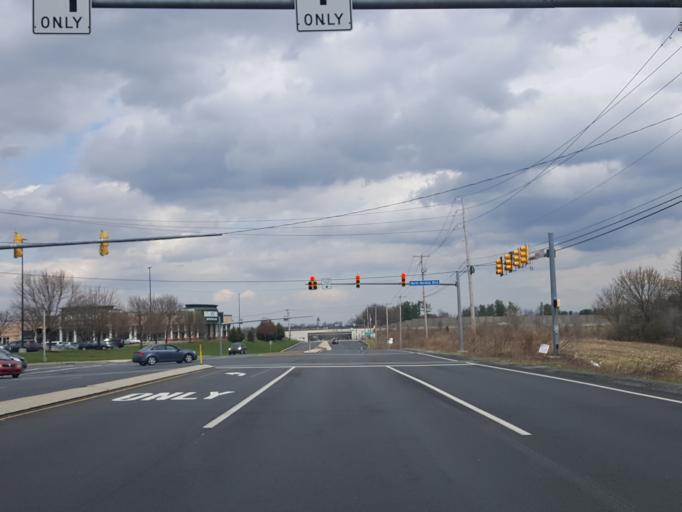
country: US
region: Pennsylvania
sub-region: Berks County
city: Spring Ridge
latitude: 40.3550
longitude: -75.9798
